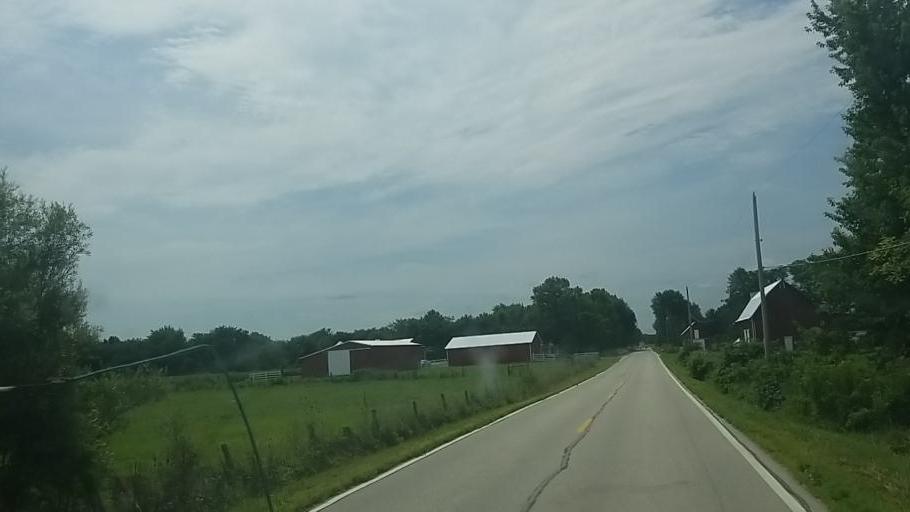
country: US
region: Ohio
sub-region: Delaware County
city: Sunbury
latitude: 40.1997
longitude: -82.8261
